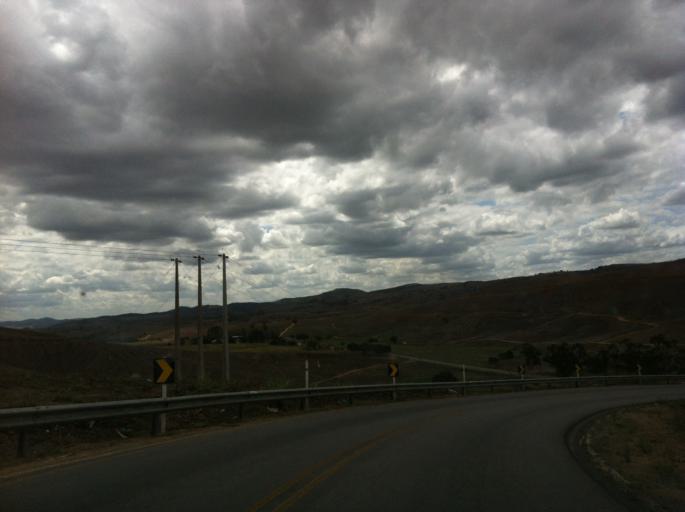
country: BR
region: Alagoas
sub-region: Ibateguara
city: Ibateguara
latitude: -8.9647
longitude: -35.9358
